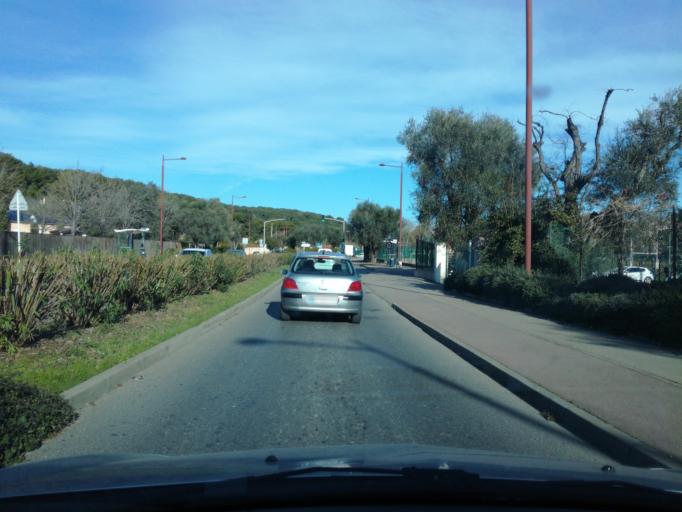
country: FR
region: Provence-Alpes-Cote d'Azur
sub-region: Departement des Alpes-Maritimes
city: Vallauris
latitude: 43.5800
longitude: 7.0898
